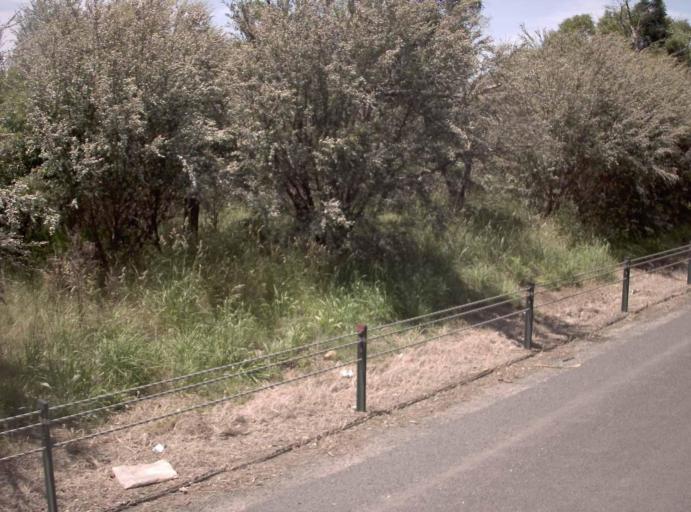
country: AU
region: Victoria
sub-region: Baw Baw
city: Warragul
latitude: -38.1753
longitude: 145.9763
